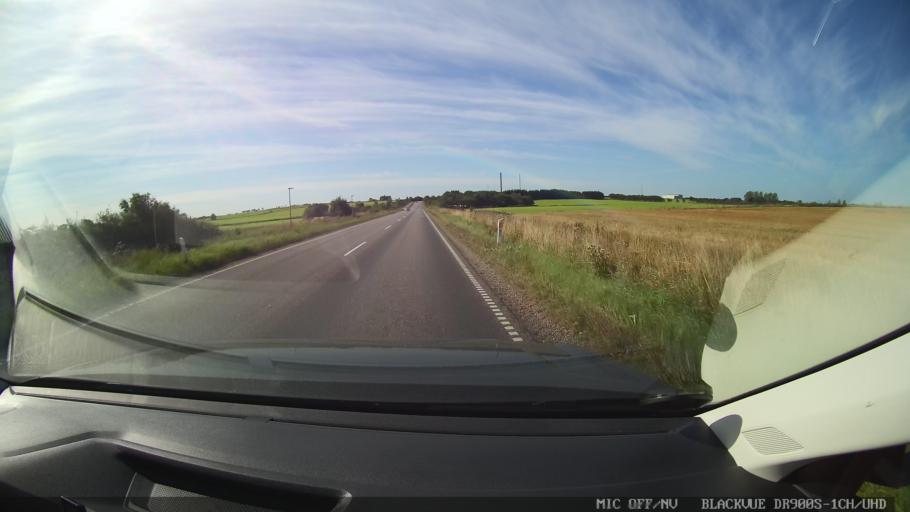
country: DK
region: North Denmark
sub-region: Mariagerfjord Kommune
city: Hobro
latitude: 56.6627
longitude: 9.8273
